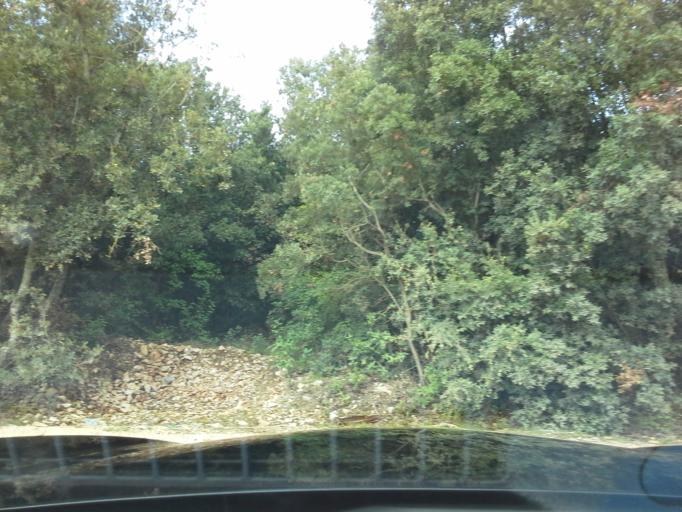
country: HR
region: Primorsko-Goranska
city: Mali Losinj
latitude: 44.5787
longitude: 14.4055
